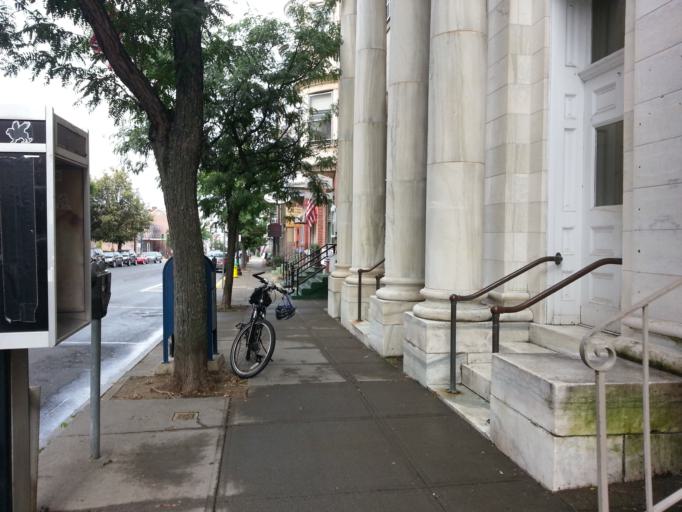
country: US
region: New York
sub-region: Columbia County
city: Oakdale
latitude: 42.2491
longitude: -73.7859
